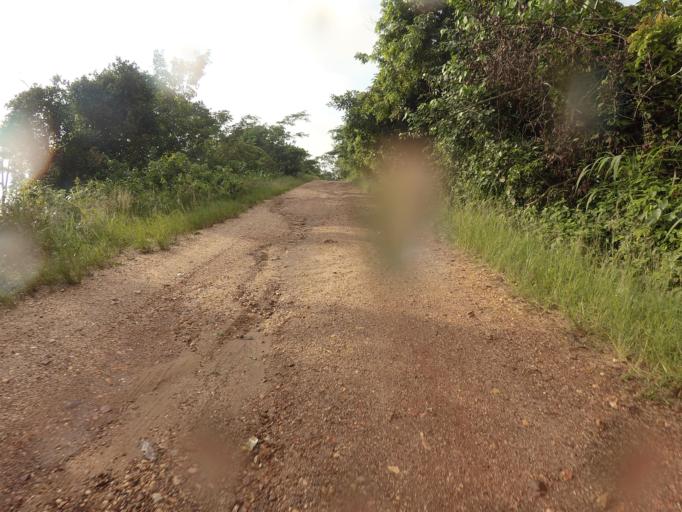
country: GH
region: Volta
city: Kpandu
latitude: 6.8432
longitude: 0.4316
